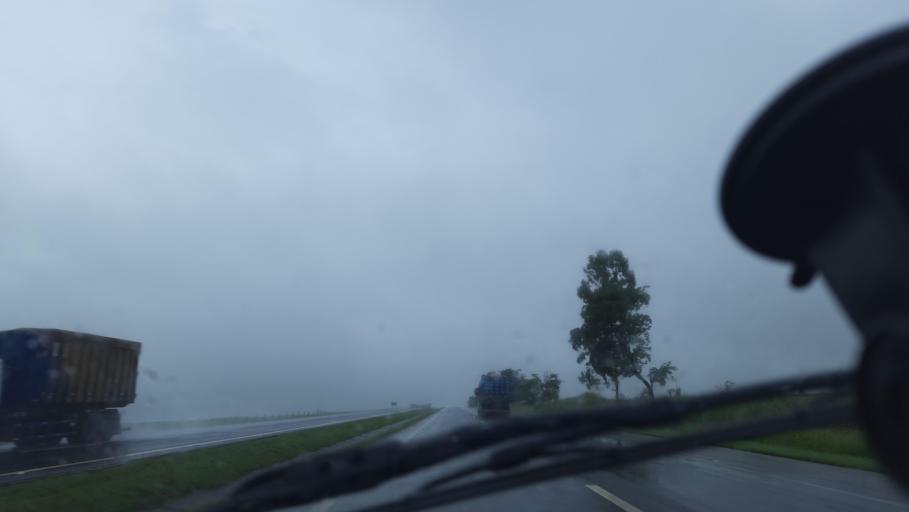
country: BR
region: Sao Paulo
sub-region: Aguai
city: Aguai
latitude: -22.0186
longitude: -47.0350
